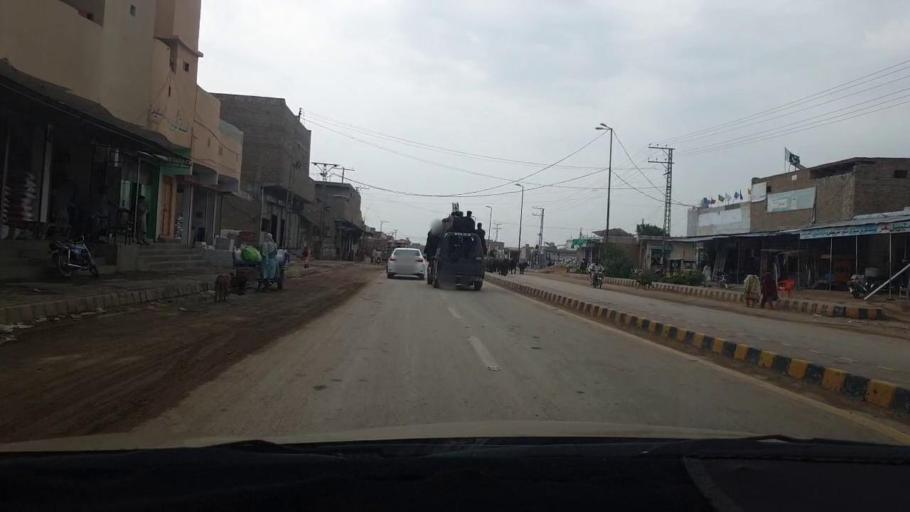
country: PK
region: Sindh
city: Larkana
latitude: 27.5763
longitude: 68.2267
